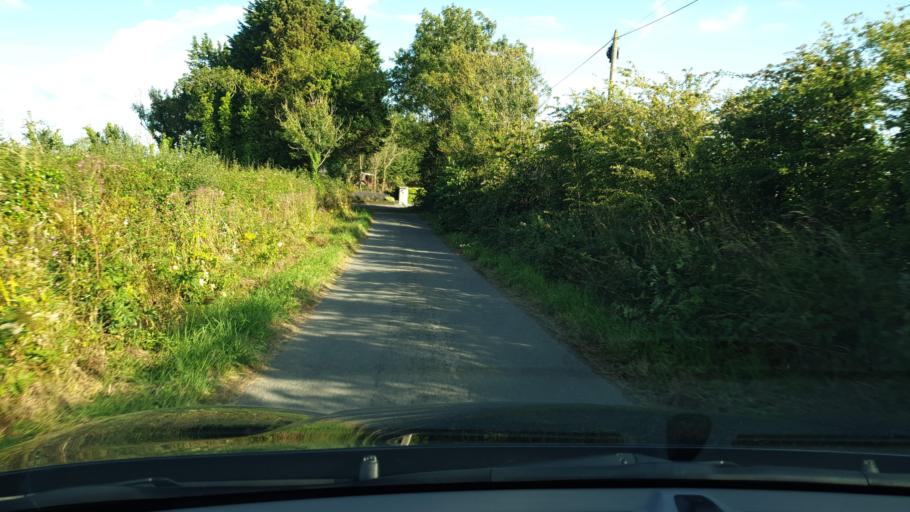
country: IE
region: Leinster
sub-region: An Mhi
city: Stamullin
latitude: 53.5928
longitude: -6.2602
